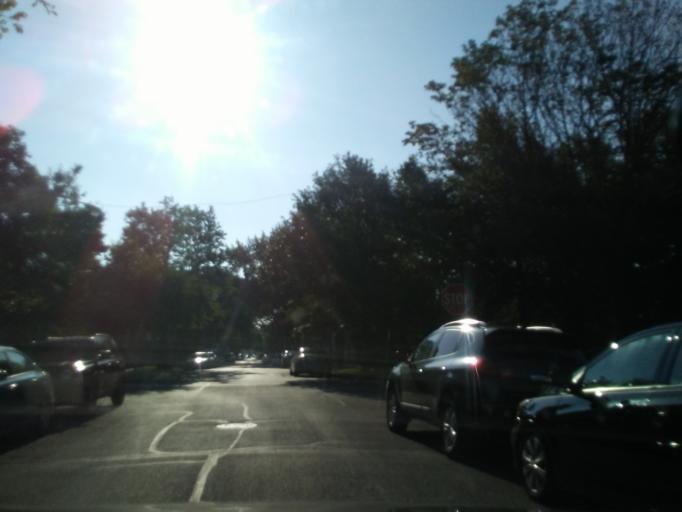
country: US
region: Illinois
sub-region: Cook County
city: Oak Park
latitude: 41.9371
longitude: -87.7411
